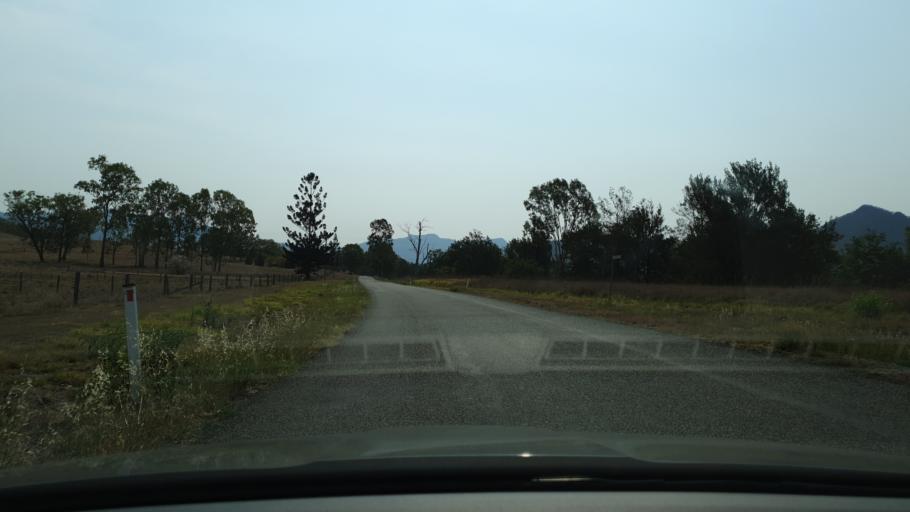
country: AU
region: Queensland
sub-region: Ipswich
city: Deebing Heights
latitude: -28.1370
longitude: 152.5933
